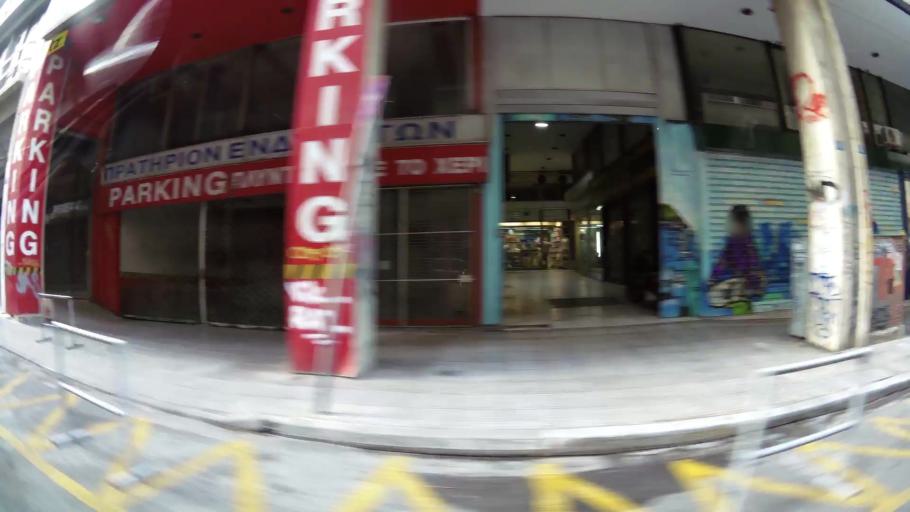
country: GR
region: Attica
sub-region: Nomarchia Athinas
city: Athens
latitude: 37.9864
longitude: 23.7303
